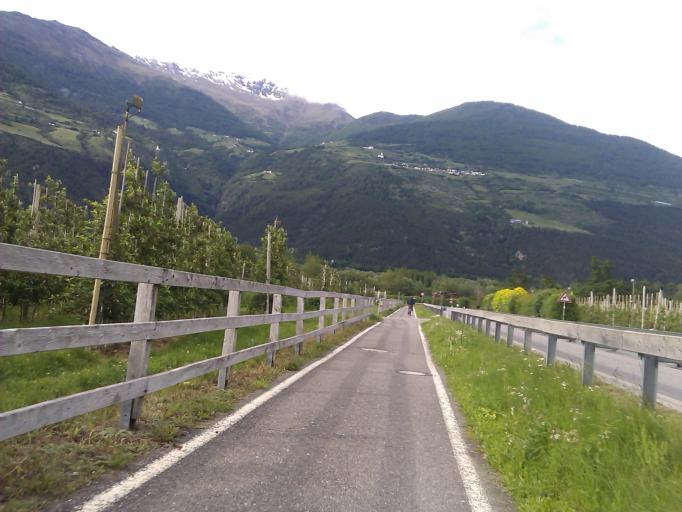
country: IT
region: Trentino-Alto Adige
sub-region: Bolzano
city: Lasa
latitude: 46.6194
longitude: 10.6464
